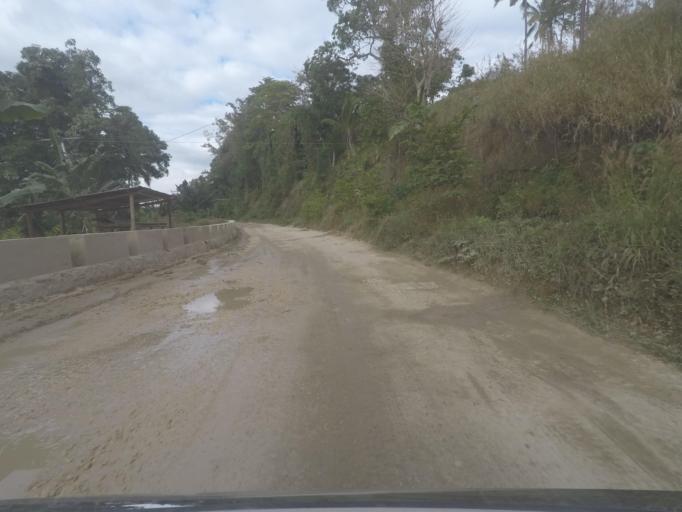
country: TL
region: Baucau
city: Venilale
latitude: -8.6015
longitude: 126.3845
